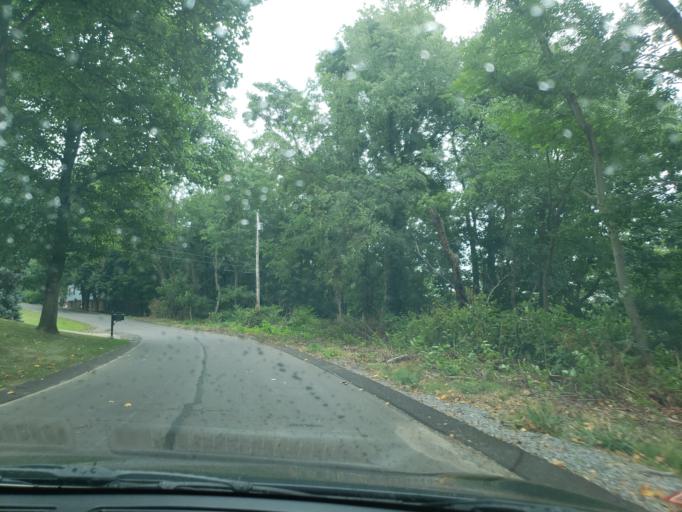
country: US
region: Pennsylvania
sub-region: Allegheny County
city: Avalon
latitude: 40.5170
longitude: -80.0675
